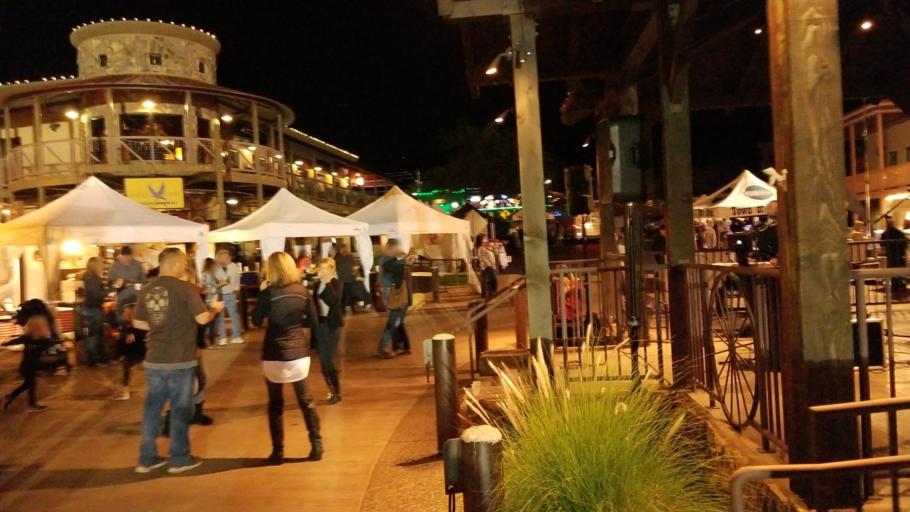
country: US
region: Arizona
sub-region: Maricopa County
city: Carefree
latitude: 33.8302
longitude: -111.9287
